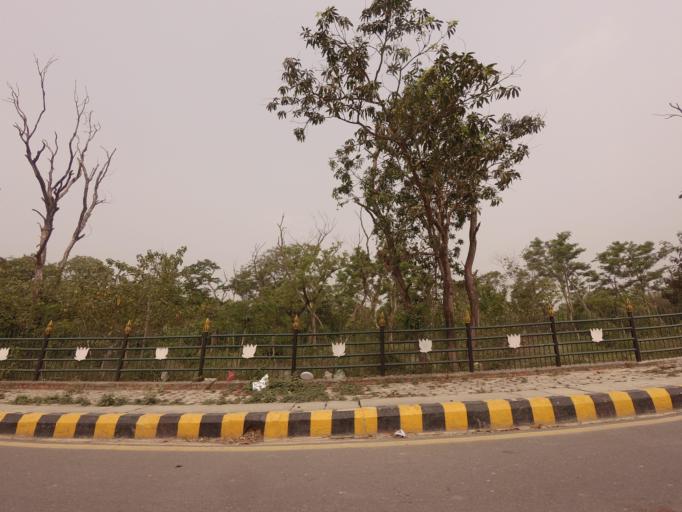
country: IN
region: Uttar Pradesh
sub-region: Maharajganj
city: Nautanwa
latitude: 27.4729
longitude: 83.2838
